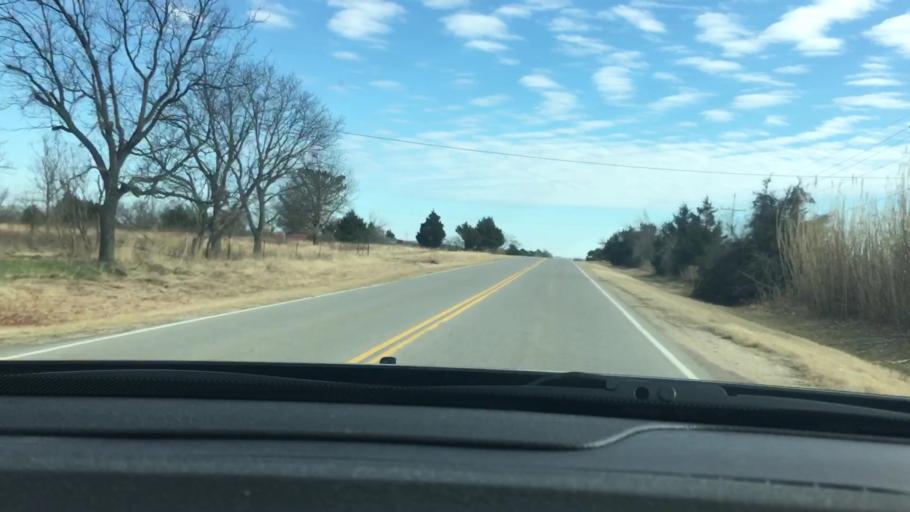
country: US
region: Oklahoma
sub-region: Pontotoc County
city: Ada
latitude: 34.7880
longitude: -96.7972
